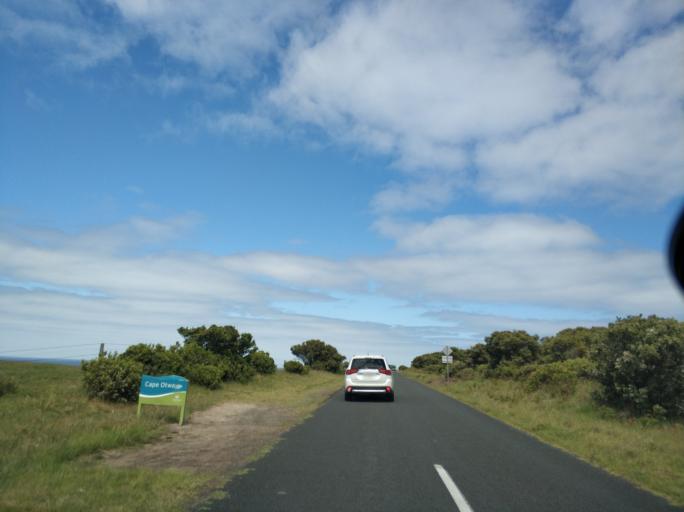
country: AU
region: Victoria
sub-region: Colac-Otway
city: Apollo Bay
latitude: -38.8496
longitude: 143.5359
